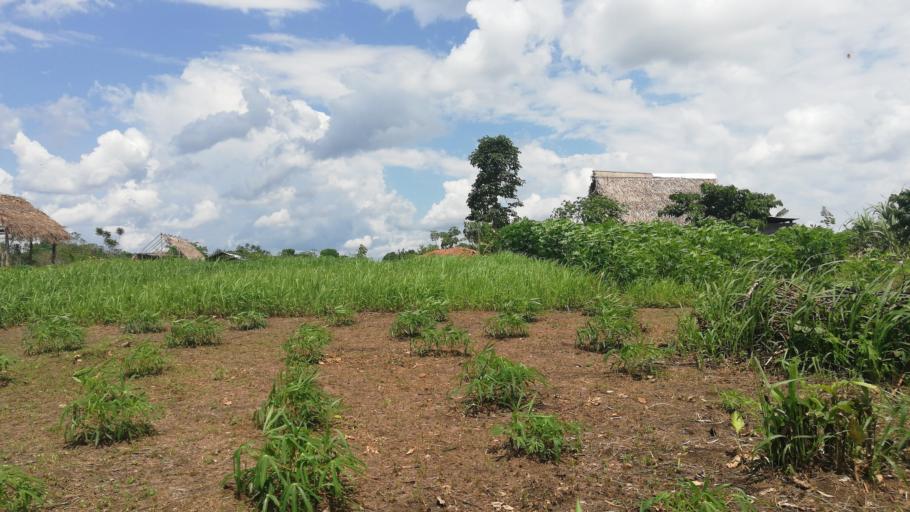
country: PE
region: Ucayali
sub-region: Provincia de Coronel Portillo
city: Puerto Callao
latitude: -8.2704
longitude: -74.6529
